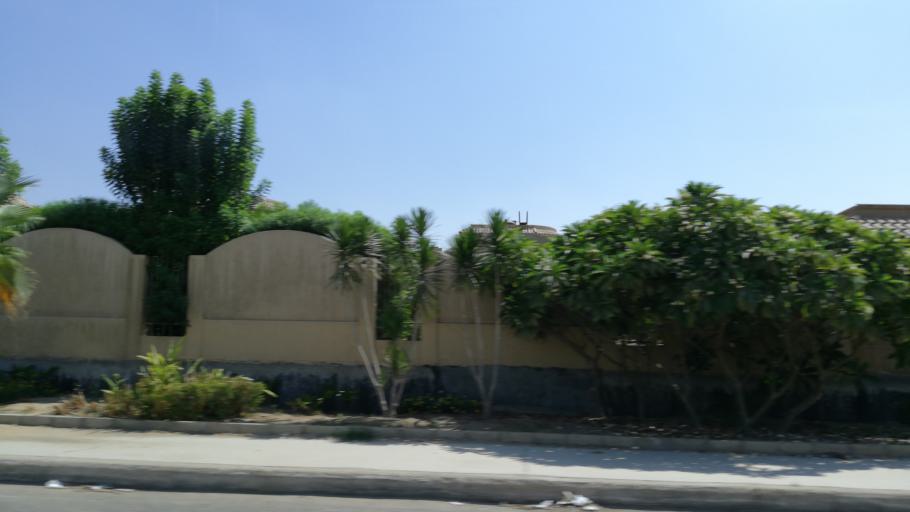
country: EG
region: Muhafazat al Qalyubiyah
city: Al Khankah
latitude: 30.0532
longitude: 31.4964
